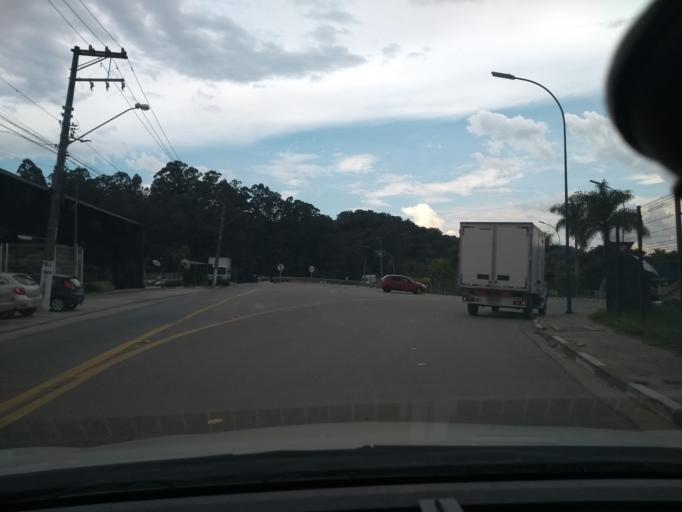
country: BR
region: Sao Paulo
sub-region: Itapevi
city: Itapevi
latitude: -23.5166
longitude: -46.9661
